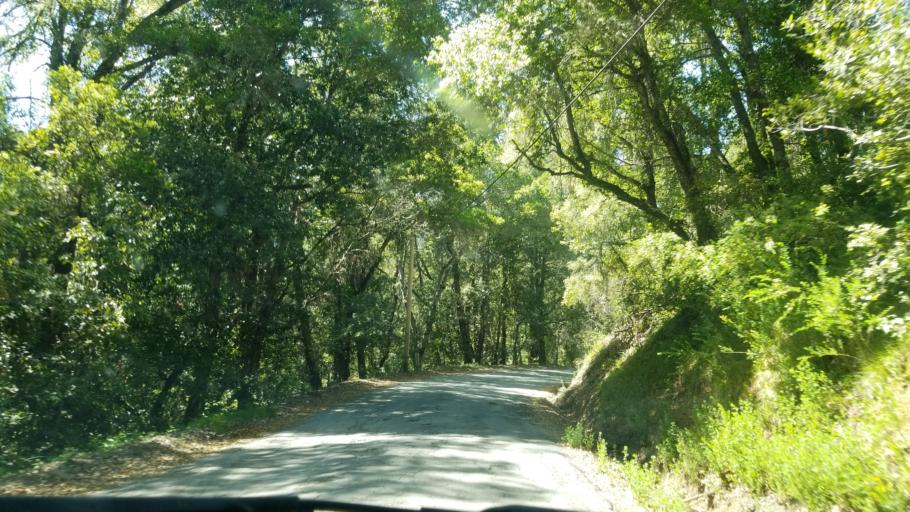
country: US
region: California
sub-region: Santa Cruz County
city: Day Valley
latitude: 37.0665
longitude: -121.8344
